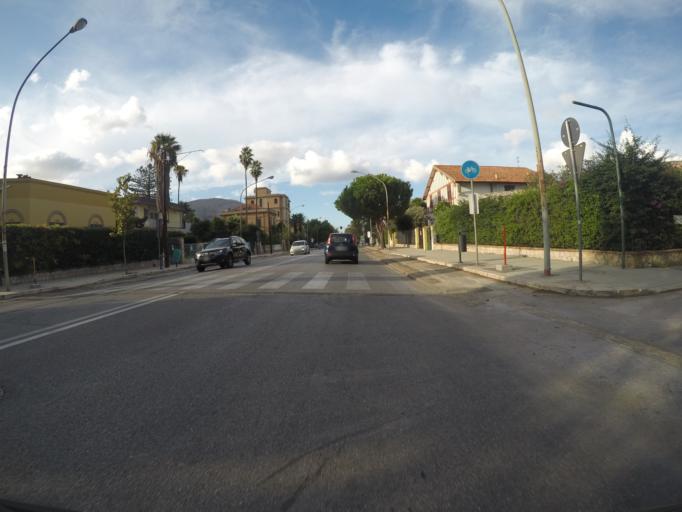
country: IT
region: Sicily
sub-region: Palermo
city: Palermo
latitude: 38.1926
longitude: 13.3325
